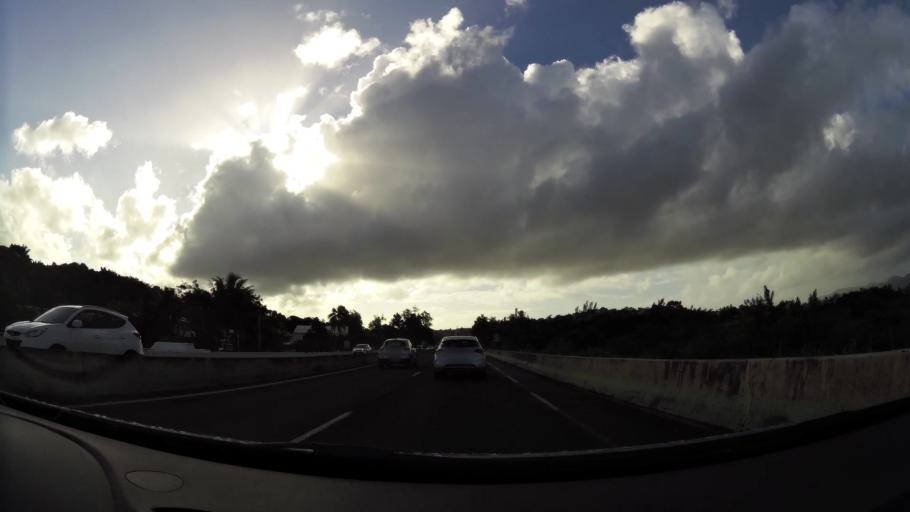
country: MQ
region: Martinique
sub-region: Martinique
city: Ducos
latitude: 14.5890
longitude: -60.9825
